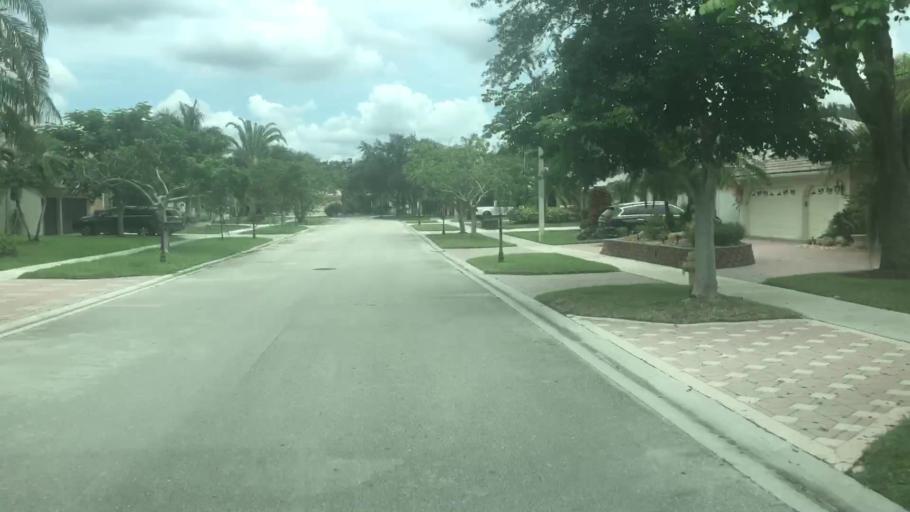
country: US
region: Florida
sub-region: Broward County
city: Cooper City
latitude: 26.0433
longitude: -80.2675
